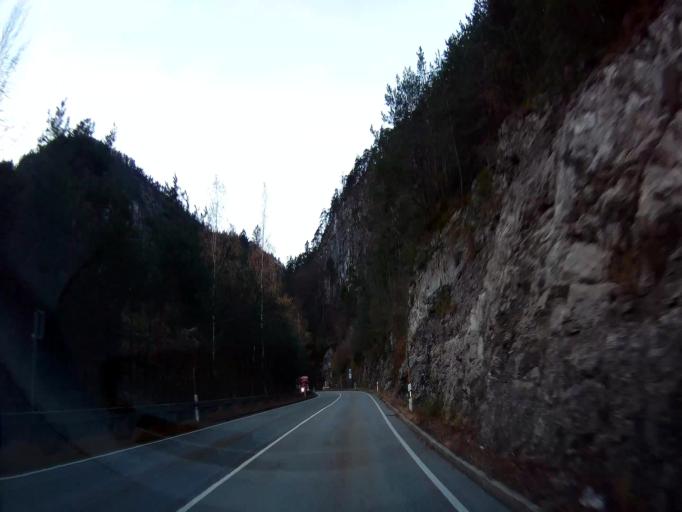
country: DE
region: Bavaria
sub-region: Upper Bavaria
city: Schneizlreuth
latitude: 47.7099
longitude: 12.8099
